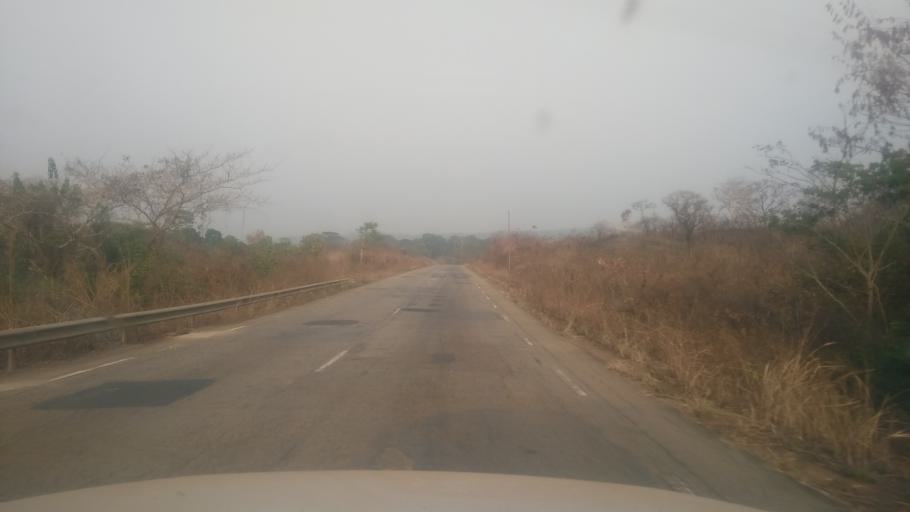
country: CM
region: Centre
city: Bafia
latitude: 4.8136
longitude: 11.0359
